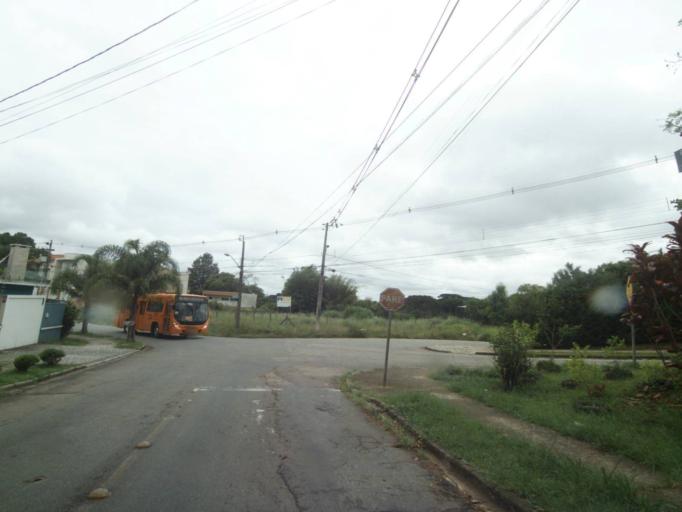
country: BR
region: Parana
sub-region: Curitiba
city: Curitiba
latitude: -25.4441
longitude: -49.3300
